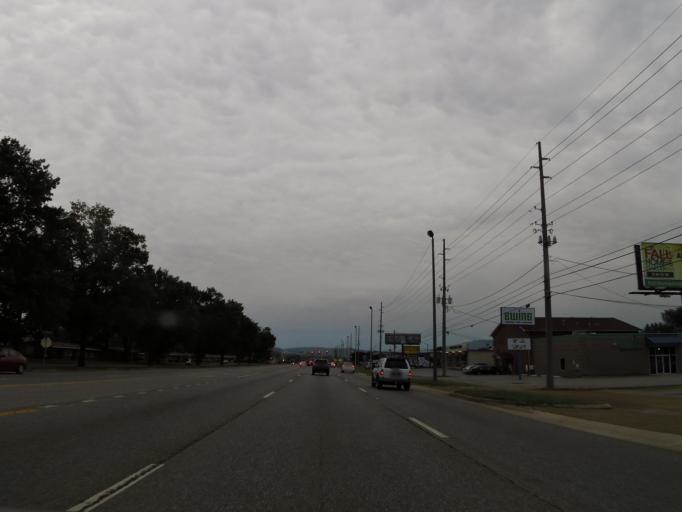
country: US
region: Alabama
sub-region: Madison County
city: Huntsville
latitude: 34.7365
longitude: -86.6084
